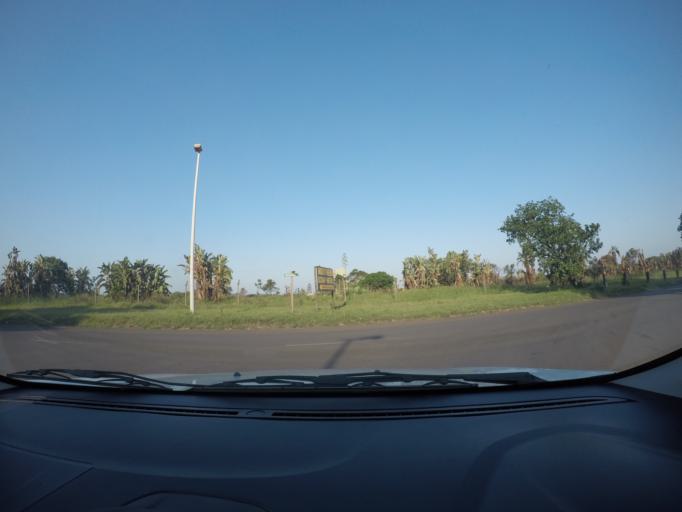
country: ZA
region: KwaZulu-Natal
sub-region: uThungulu District Municipality
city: Richards Bay
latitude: -28.7637
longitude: 32.0074
